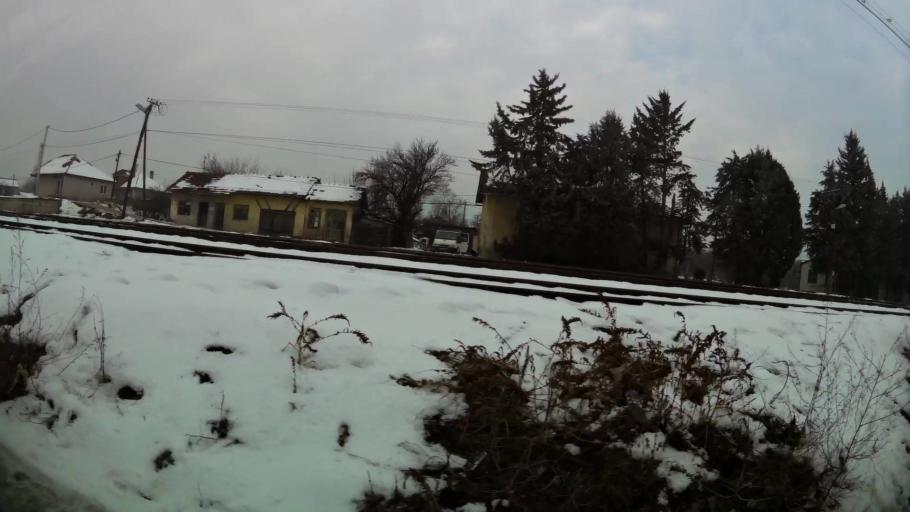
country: MK
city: Kondovo
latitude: 42.0462
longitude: 21.3539
